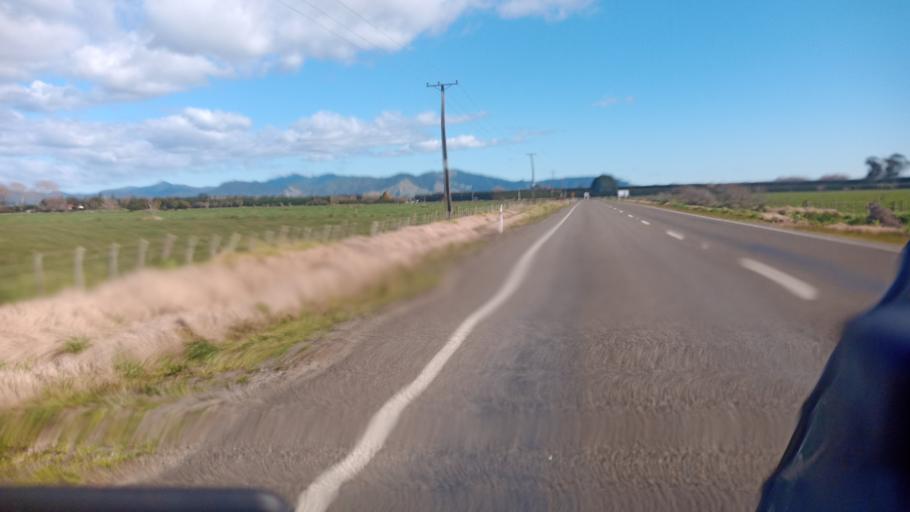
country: NZ
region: Bay of Plenty
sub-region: Opotiki District
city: Opotiki
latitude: -37.9959
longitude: 177.3014
